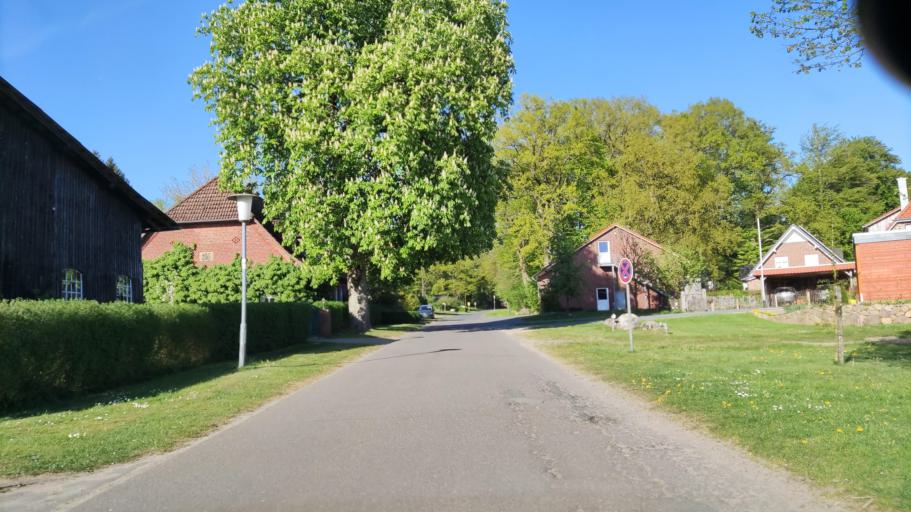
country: DE
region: Lower Saxony
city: Soderstorf
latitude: 53.1608
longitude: 10.1523
